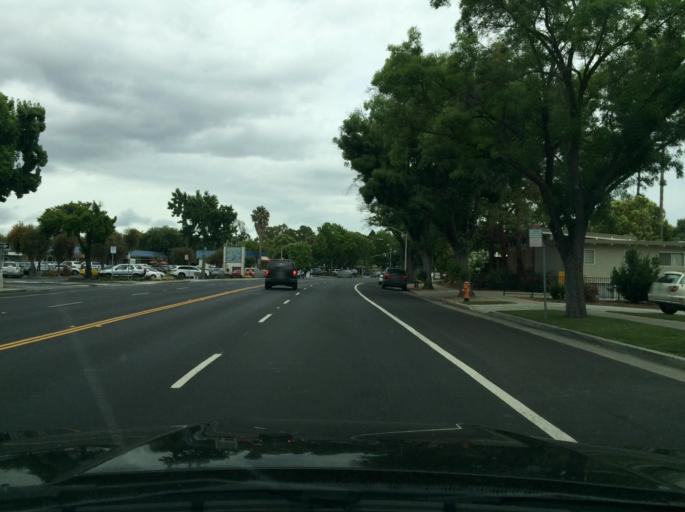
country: US
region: California
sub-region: Santa Clara County
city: Los Altos
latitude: 37.4189
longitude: -122.1086
